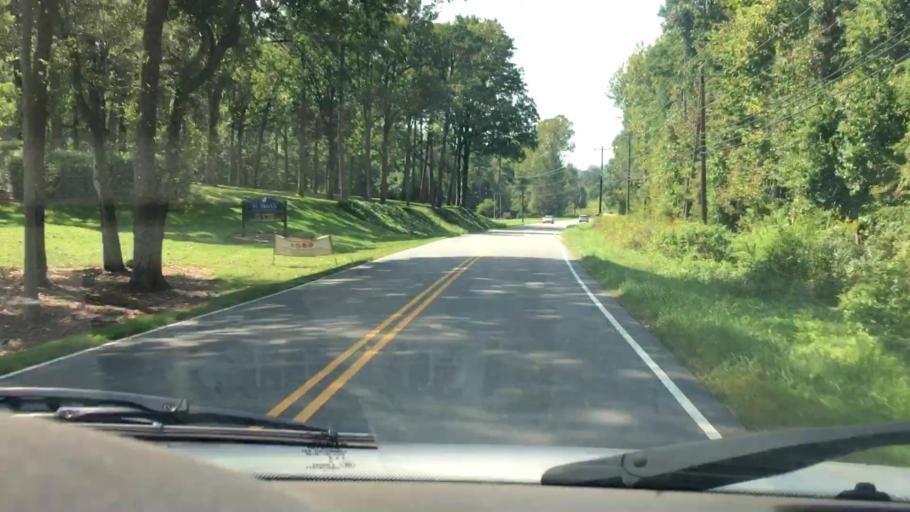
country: US
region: North Carolina
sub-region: Mecklenburg County
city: Huntersville
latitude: 35.3489
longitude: -80.8810
